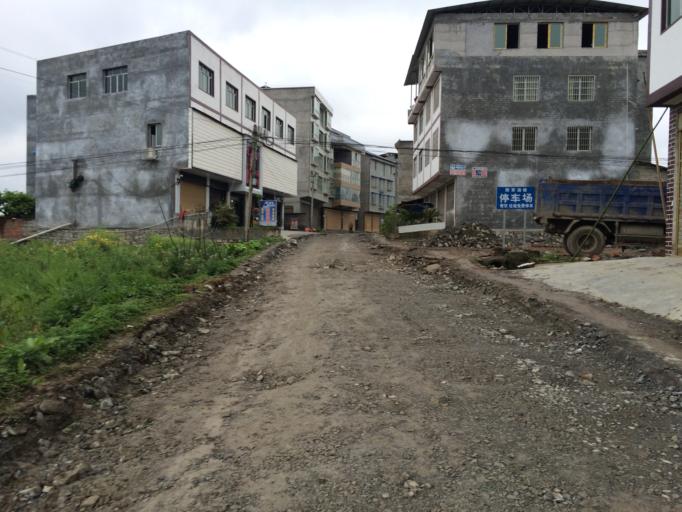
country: CN
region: Guizhou Sheng
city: Dalucao
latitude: 27.8304
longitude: 107.2533
